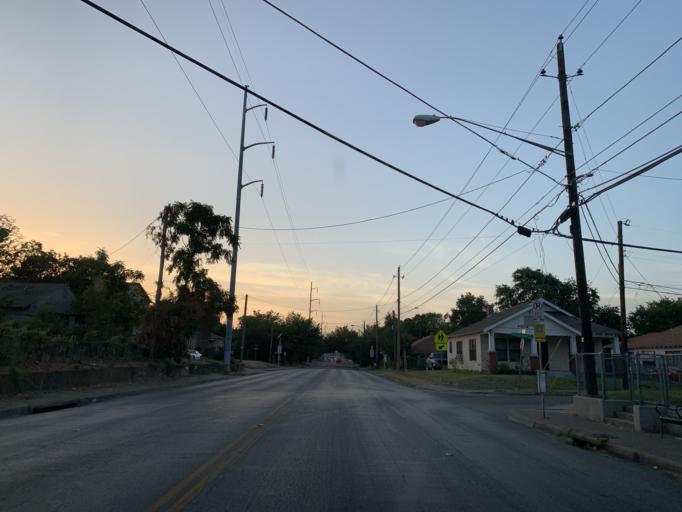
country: US
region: Texas
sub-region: Dallas County
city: Dallas
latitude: 32.7638
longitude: -96.7621
